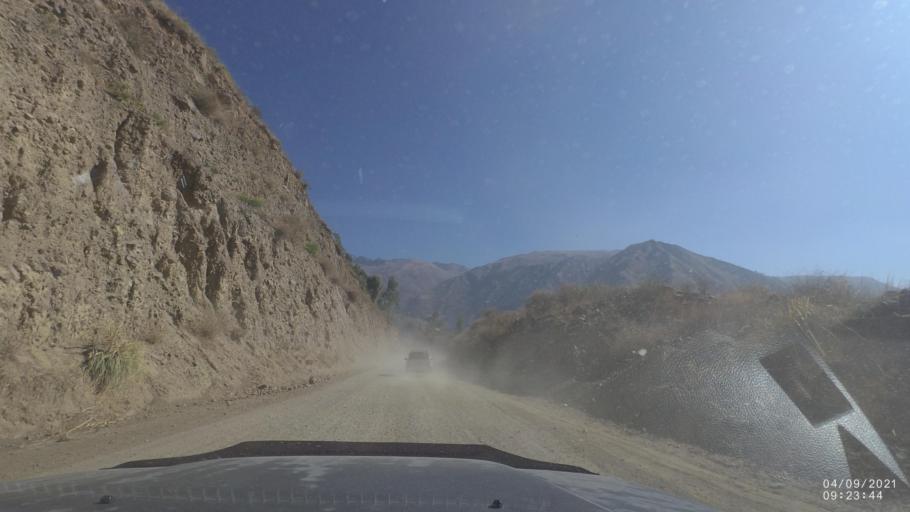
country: BO
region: Cochabamba
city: Sipe Sipe
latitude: -17.3624
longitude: -66.3671
